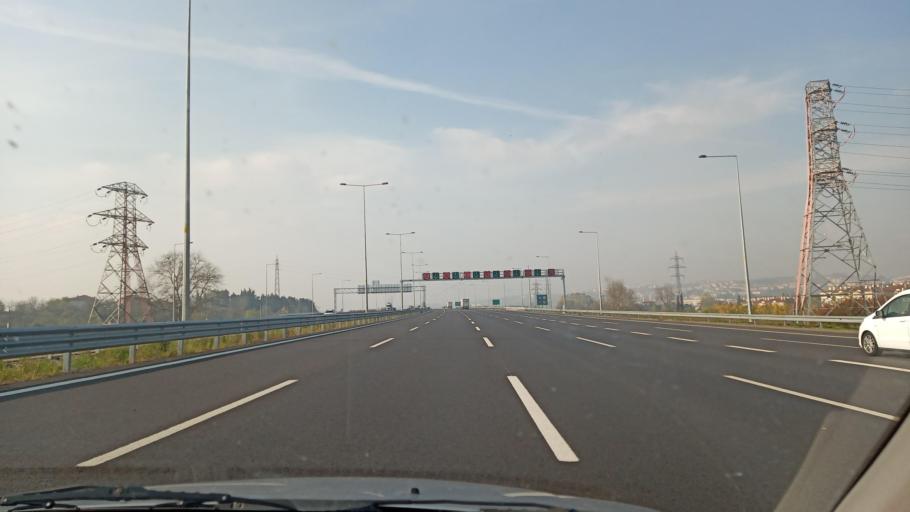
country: TR
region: Sakarya
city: Kazimpasa
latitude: 40.8437
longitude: 30.3381
